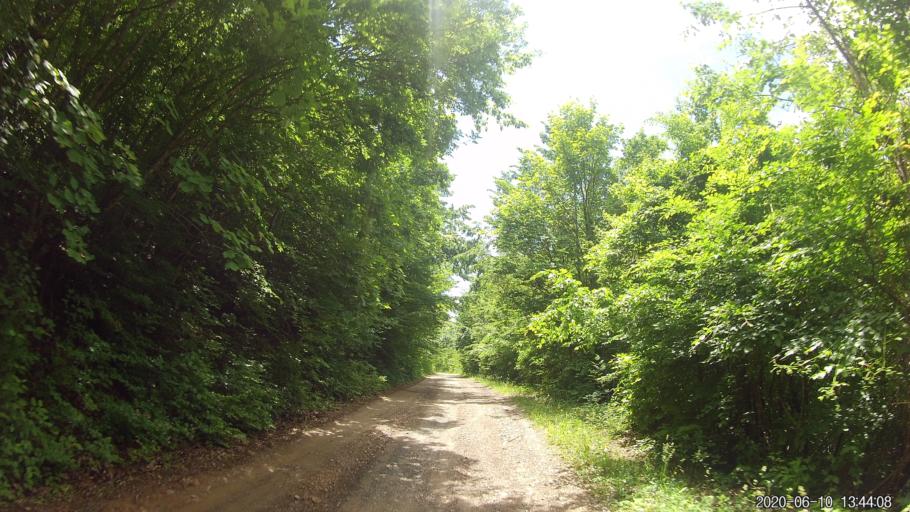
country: XK
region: Prizren
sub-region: Komuna e Therandes
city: Budakovo
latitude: 42.4150
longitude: 20.9170
